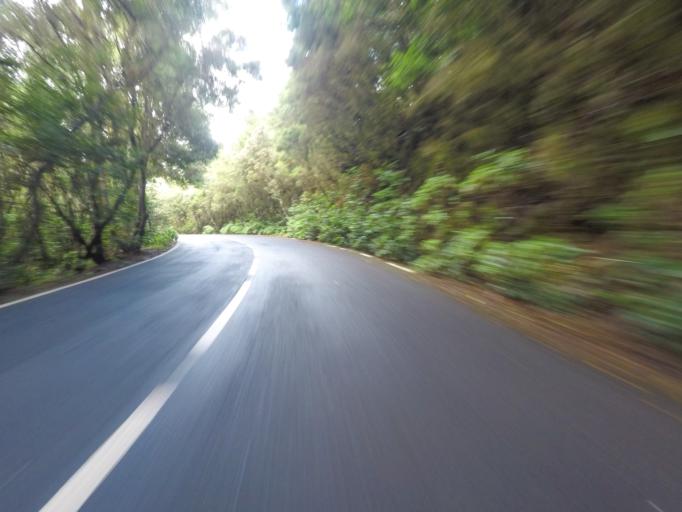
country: ES
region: Canary Islands
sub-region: Provincia de Santa Cruz de Tenerife
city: Alajero
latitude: 28.1153
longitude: -17.2185
